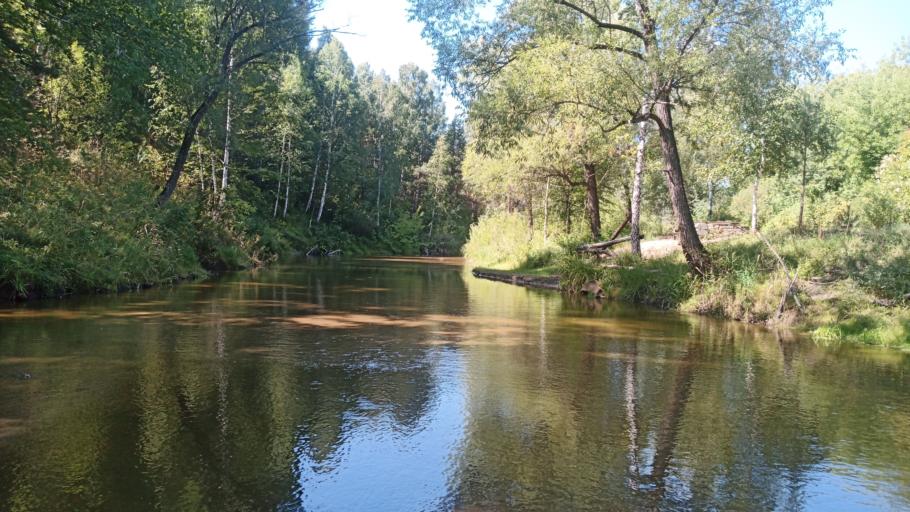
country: RU
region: Altai Krai
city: Yuzhnyy
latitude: 53.2953
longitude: 83.6835
